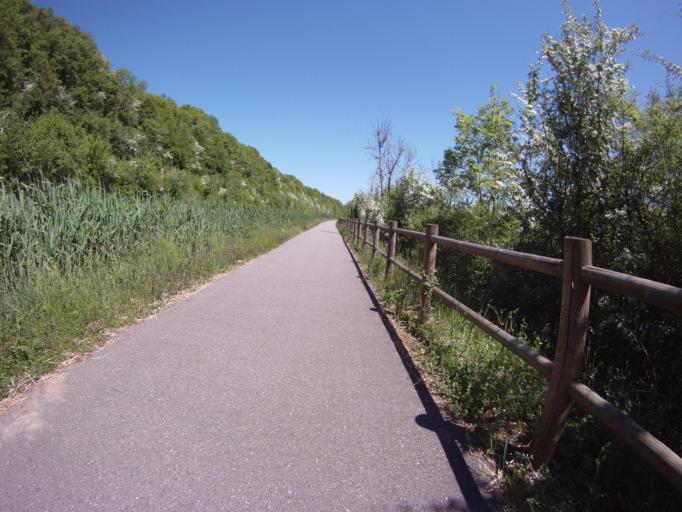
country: FR
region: Lorraine
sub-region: Departement de Meurthe-et-Moselle
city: Villey-Saint-Etienne
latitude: 48.7377
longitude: 5.9879
